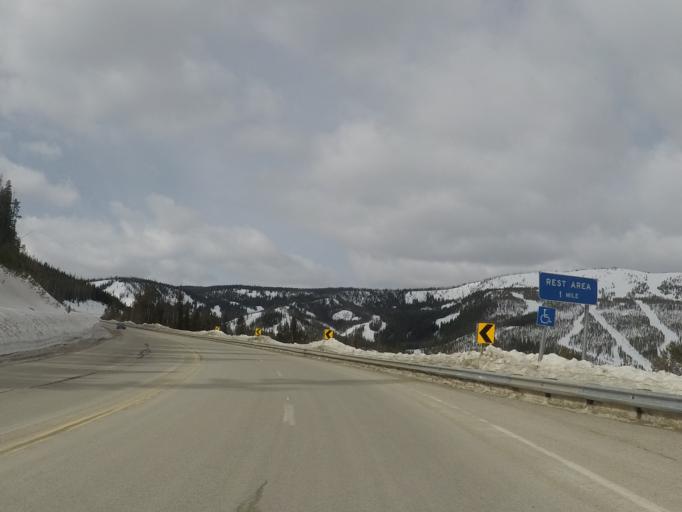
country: US
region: Idaho
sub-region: Lemhi County
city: Salmon
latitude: 45.7045
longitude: -113.9369
